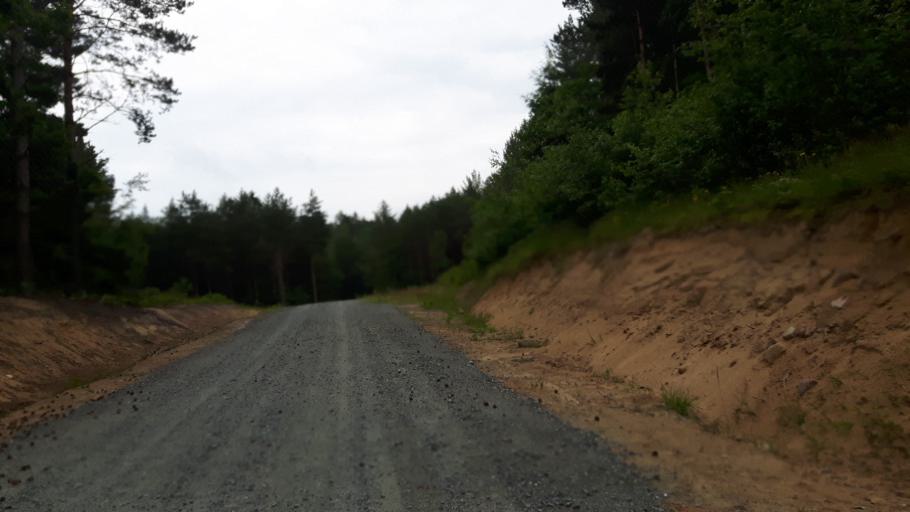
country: PL
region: Warmian-Masurian Voivodeship
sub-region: Powiat braniewski
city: Frombork
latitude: 54.3123
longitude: 19.6299
